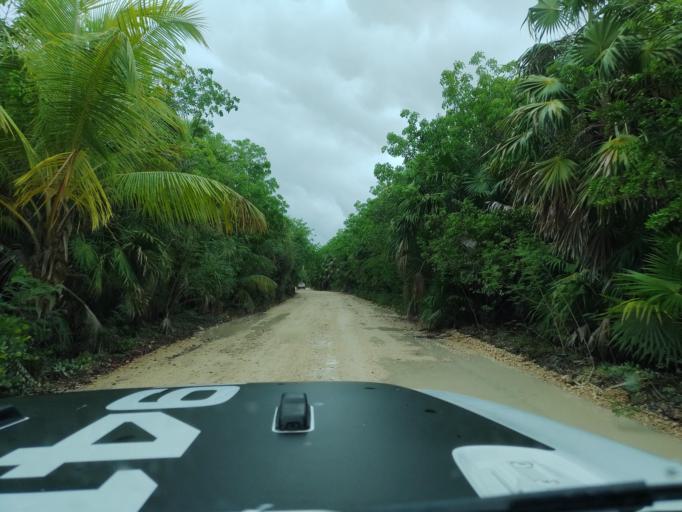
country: MX
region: Quintana Roo
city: Tulum
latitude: 20.0628
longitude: -87.4804
